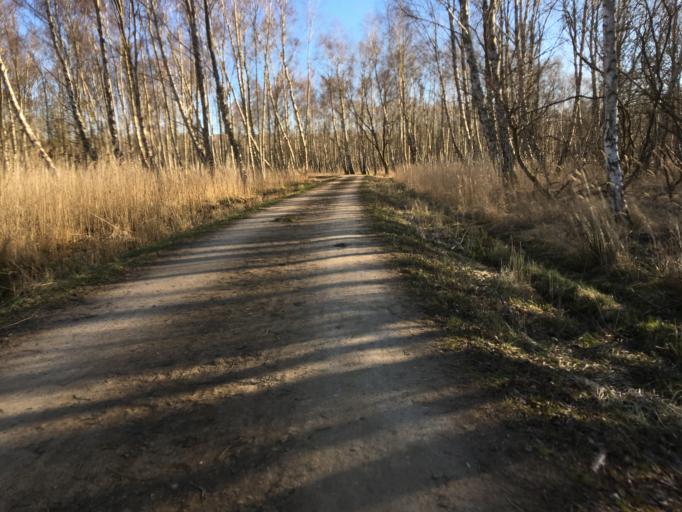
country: DK
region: Capital Region
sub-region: Tarnby Kommune
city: Tarnby
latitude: 55.5905
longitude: 12.5566
